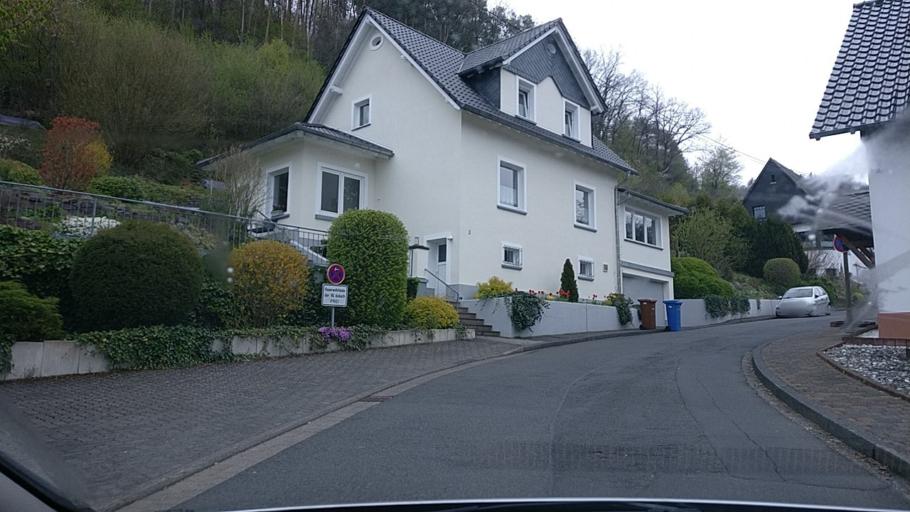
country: DE
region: Rheinland-Pfalz
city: Breitscheid
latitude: 50.6192
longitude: 7.4289
